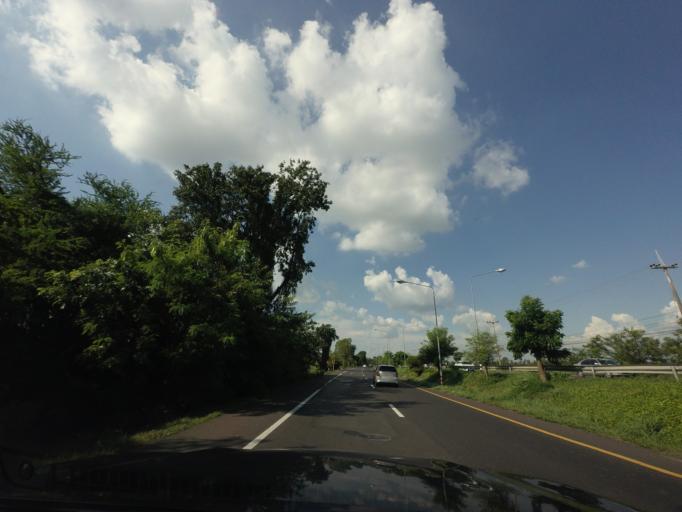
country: TH
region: Nakhon Ratchasima
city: Bua Lai
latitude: 15.6830
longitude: 102.5774
